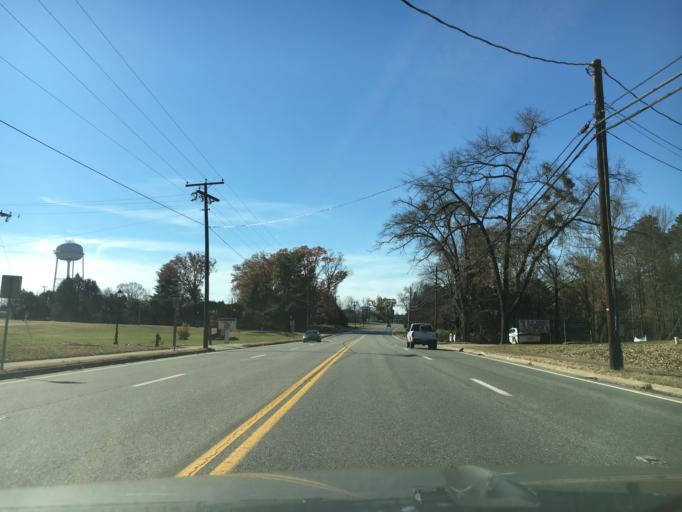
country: US
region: Virginia
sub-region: Cumberland County
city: Cumberland
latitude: 37.4934
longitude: -78.2484
